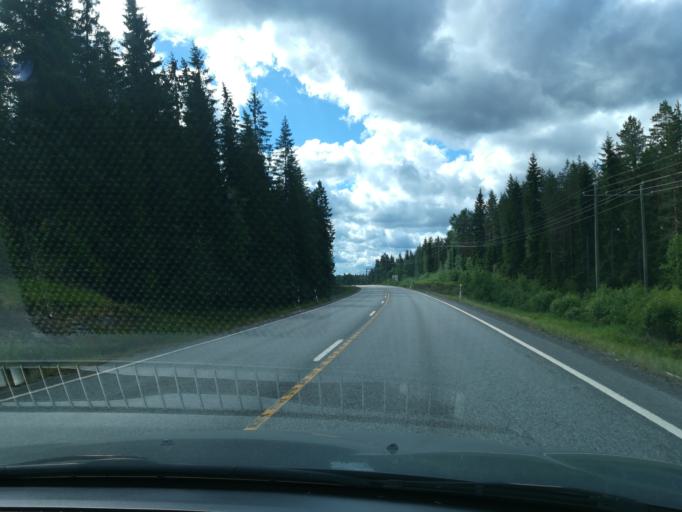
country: FI
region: Southern Savonia
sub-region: Mikkeli
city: Ristiina
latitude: 61.4630
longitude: 27.2539
